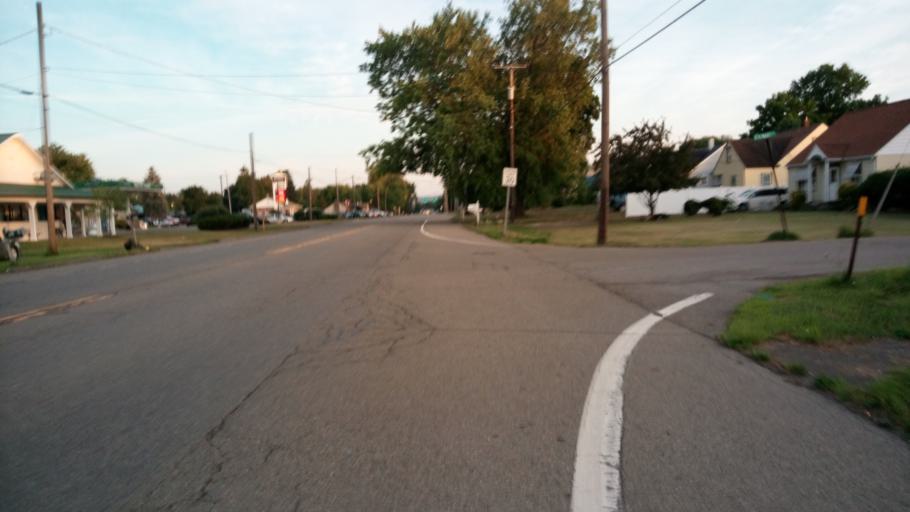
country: US
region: New York
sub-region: Chemung County
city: Elmira Heights
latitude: 42.1445
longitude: -76.8207
